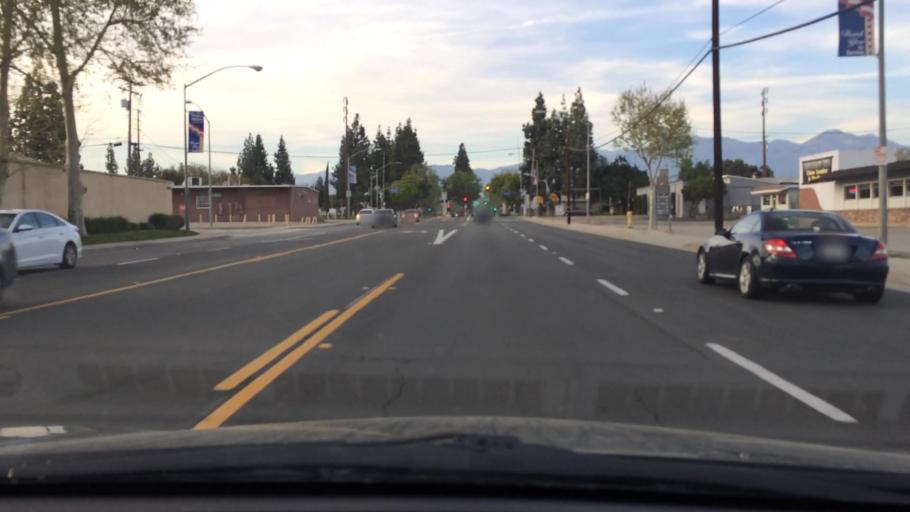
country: US
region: California
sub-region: San Bernardino County
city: Chino
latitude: 34.0104
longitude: -117.6892
